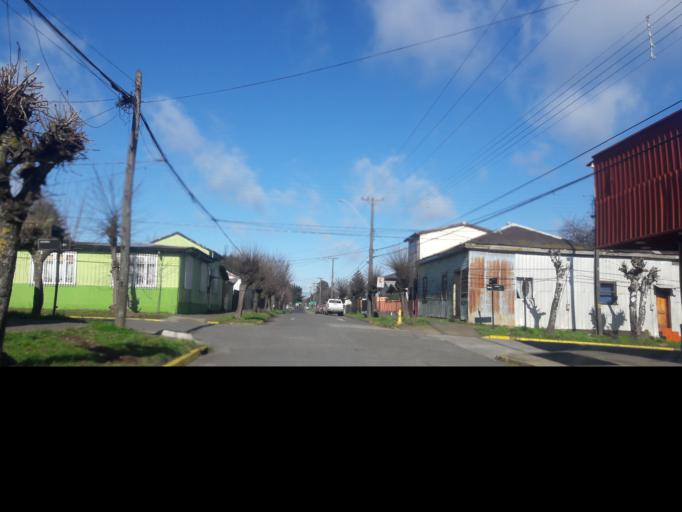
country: CL
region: Araucania
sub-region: Provincia de Malleco
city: Victoria
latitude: -38.2374
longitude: -72.3294
